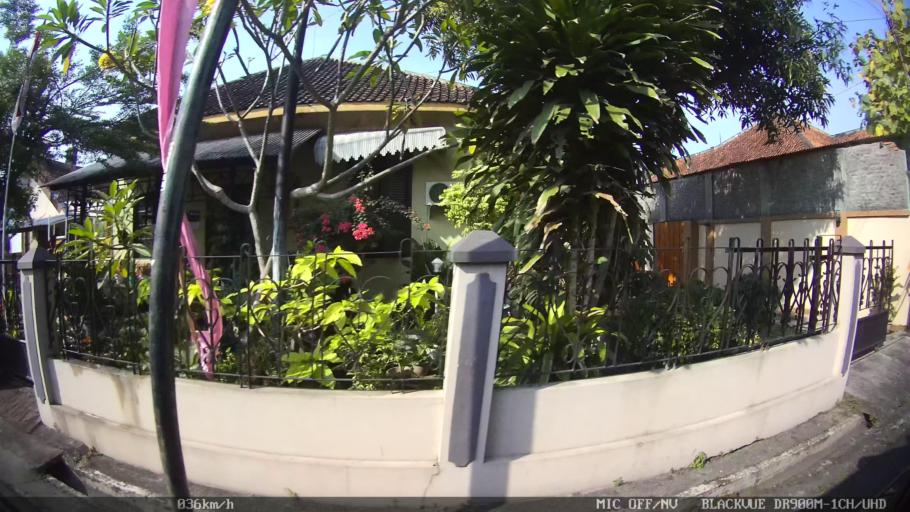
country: ID
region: Daerah Istimewa Yogyakarta
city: Yogyakarta
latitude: -7.7870
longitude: 110.3612
